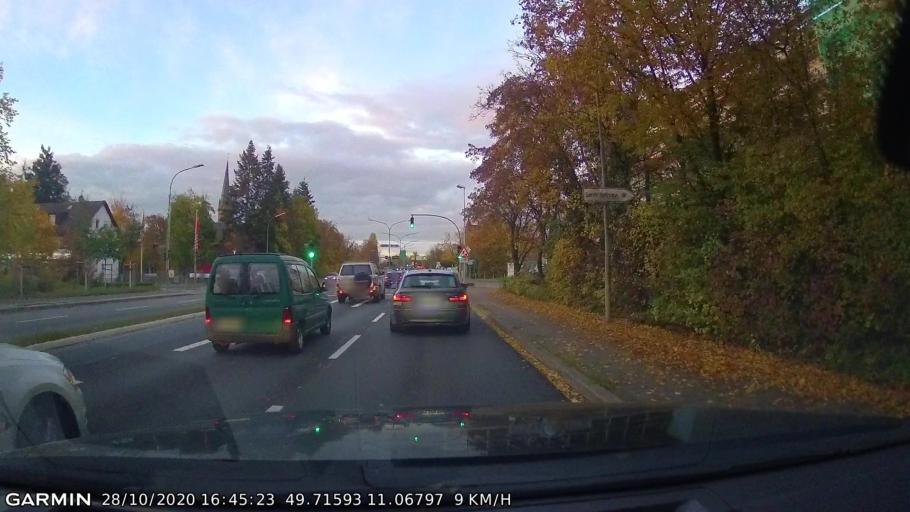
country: DE
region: Bavaria
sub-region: Upper Franconia
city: Forchheim
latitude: 49.7159
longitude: 11.0680
